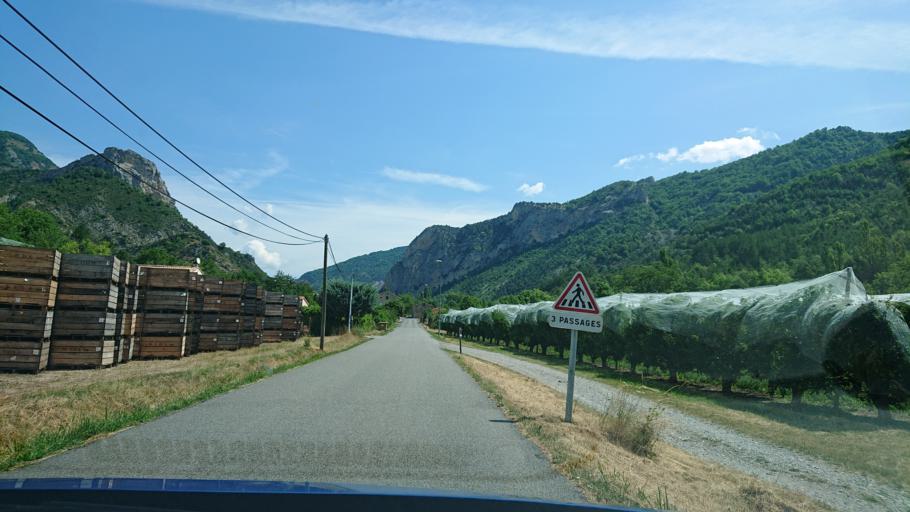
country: FR
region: Provence-Alpes-Cote d'Azur
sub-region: Departement des Hautes-Alpes
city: Tallard
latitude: 44.3668
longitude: 6.0565
